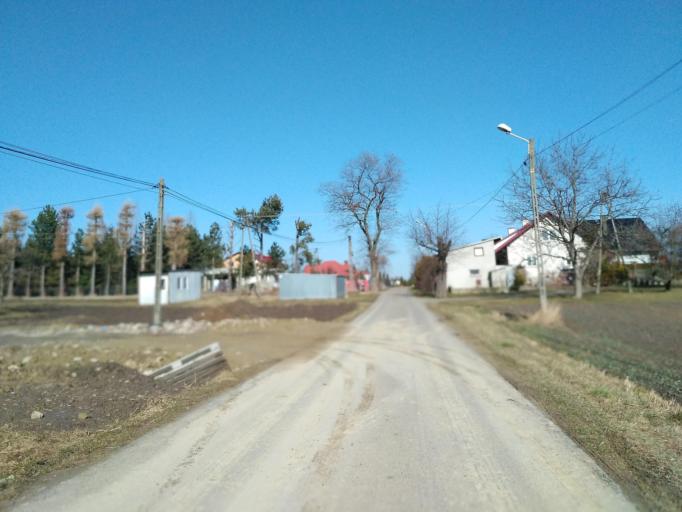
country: PL
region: Subcarpathian Voivodeship
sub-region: Powiat rzeszowski
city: Lutoryz
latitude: 49.9669
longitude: 21.9186
